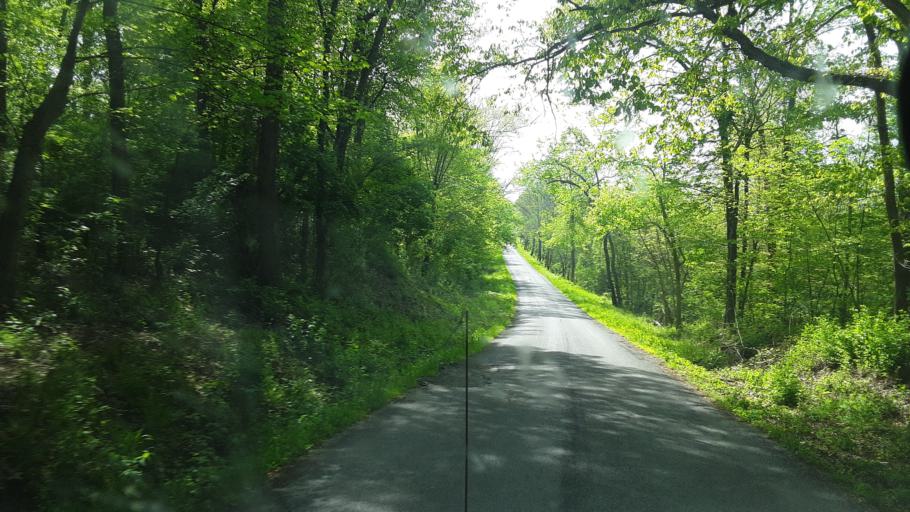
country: US
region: Illinois
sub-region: Jackson County
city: Carbondale
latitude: 37.6808
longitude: -89.2857
